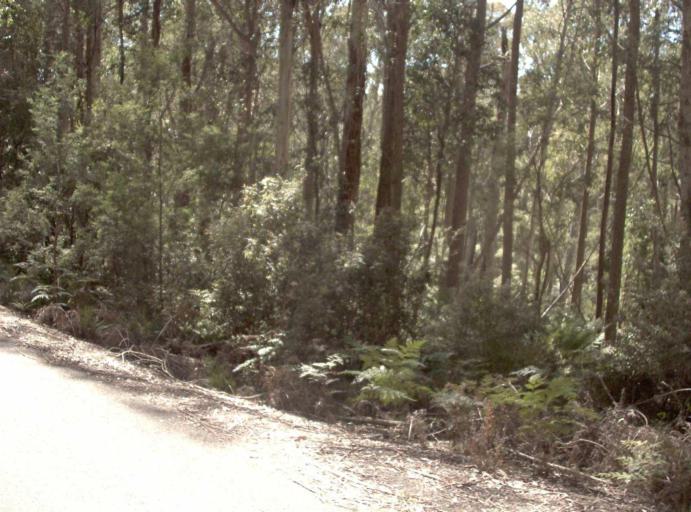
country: AU
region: New South Wales
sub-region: Bombala
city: Bombala
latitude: -37.0687
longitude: 148.7890
